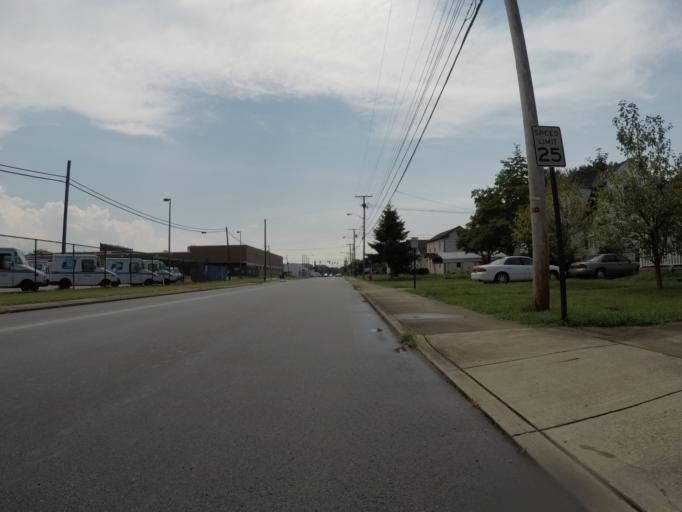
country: US
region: Kentucky
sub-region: Boyd County
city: Ashland
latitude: 38.4799
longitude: -82.6472
